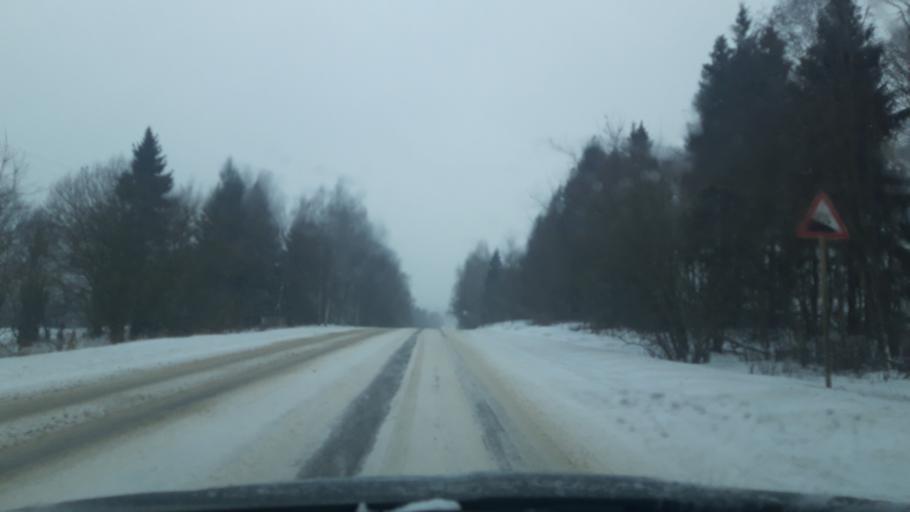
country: RU
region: Moskovskaya
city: Avtopoligon
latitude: 56.2435
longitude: 37.2419
